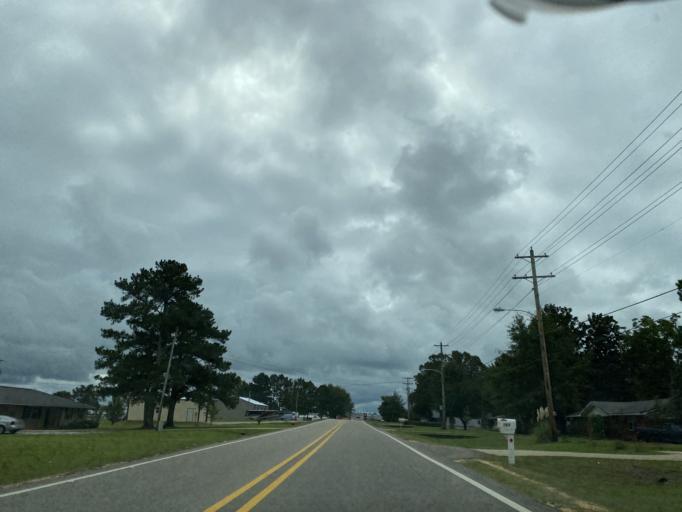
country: US
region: Mississippi
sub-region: Tishomingo County
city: Belmont
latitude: 34.4912
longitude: -88.2077
